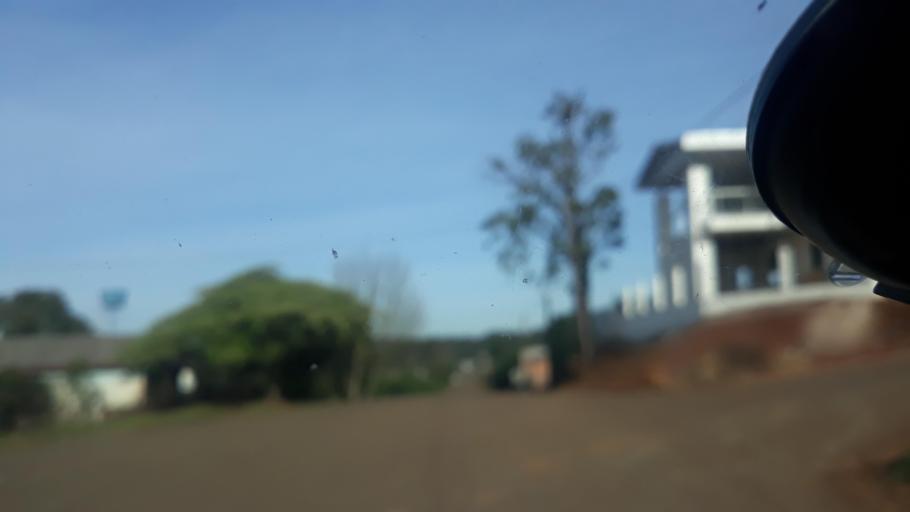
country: AR
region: Misiones
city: Bernardo de Irigoyen
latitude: -26.2638
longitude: -53.6489
